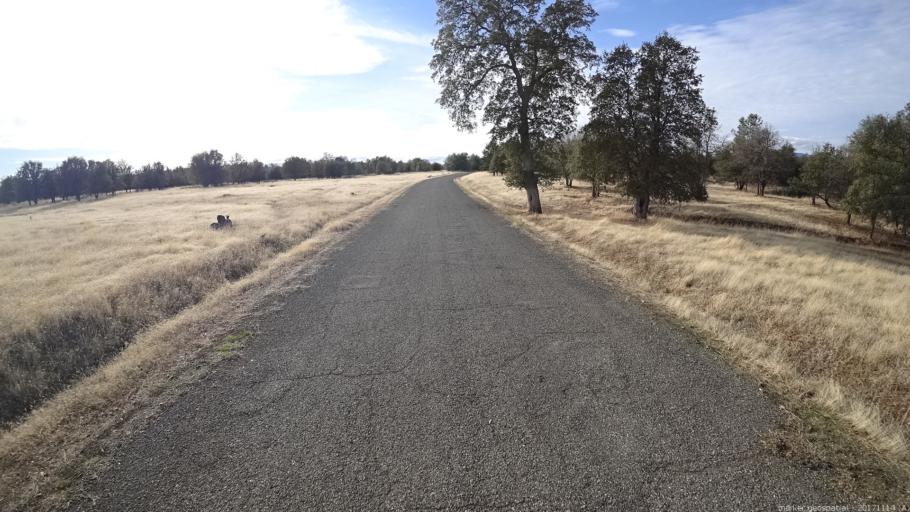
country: US
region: California
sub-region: Shasta County
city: Shasta
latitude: 40.3850
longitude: -122.5495
